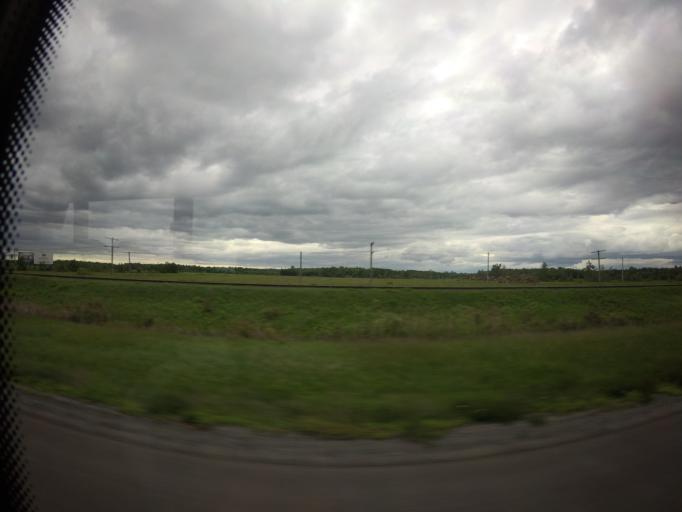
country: CA
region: Quebec
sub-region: Chaudiere-Appalaches
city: Saint-Antoine-de-Tilly
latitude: 46.5658
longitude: -71.5805
